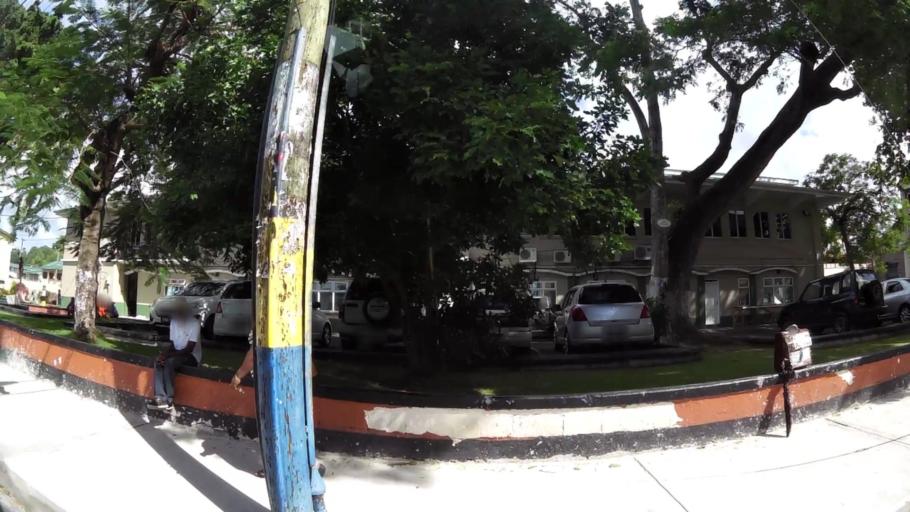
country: LC
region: Castries Quarter
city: Castries
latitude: 14.0096
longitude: -60.9903
